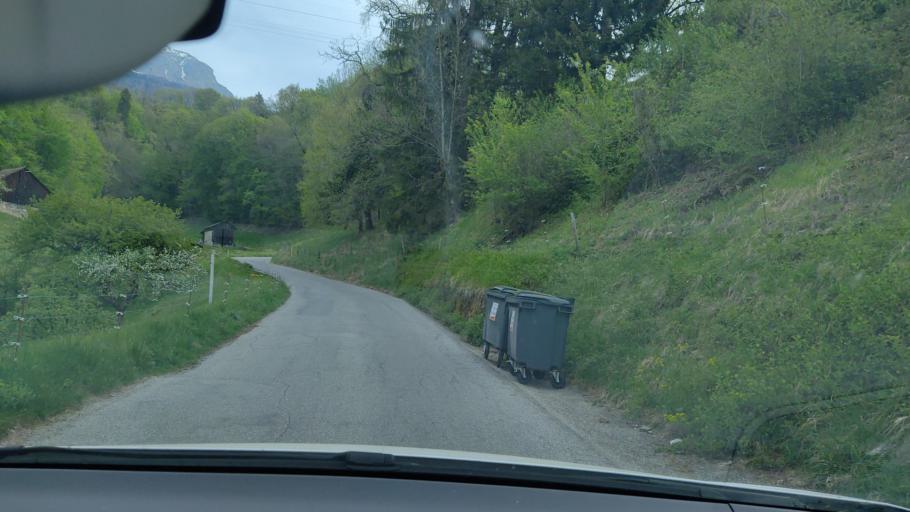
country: FR
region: Rhone-Alpes
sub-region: Departement de la Savoie
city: Ugine
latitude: 45.7611
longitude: 6.4172
